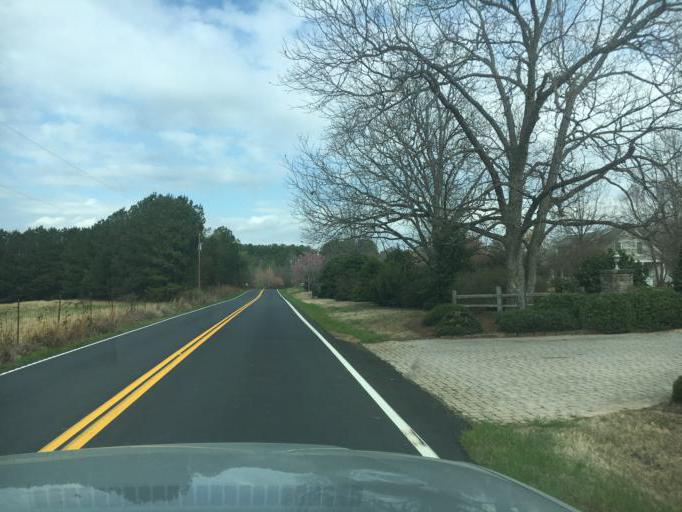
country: US
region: South Carolina
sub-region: Spartanburg County
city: Landrum
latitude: 35.1026
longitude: -82.2091
